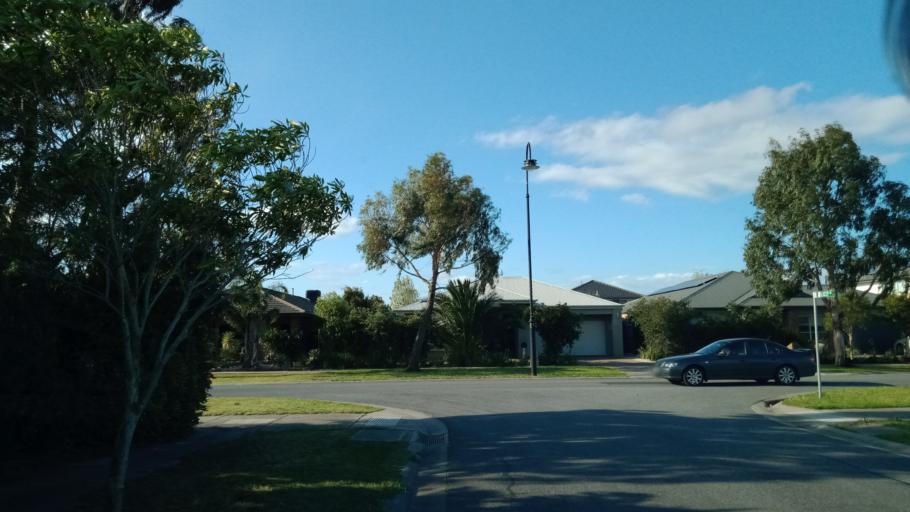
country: AU
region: Victoria
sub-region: Casey
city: Lynbrook
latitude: -38.0765
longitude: 145.2467
